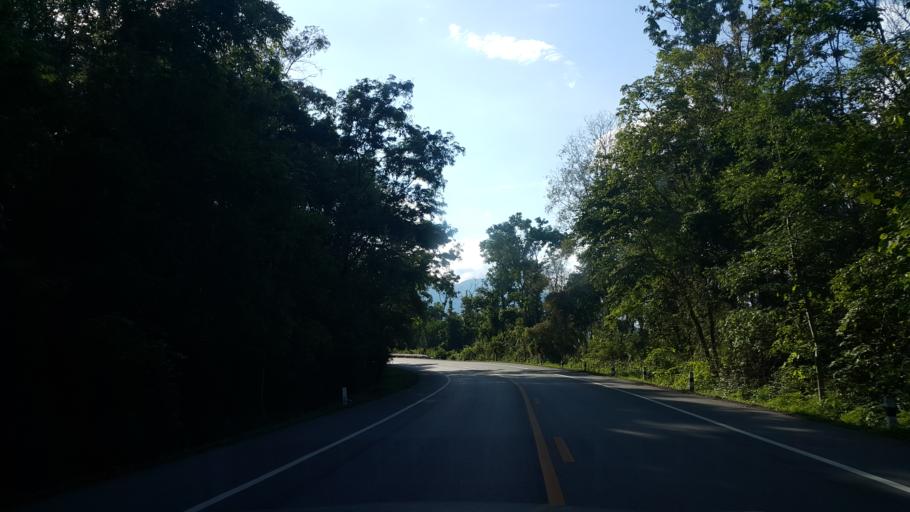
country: TH
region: Phayao
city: Phayao
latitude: 19.0887
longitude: 99.8136
